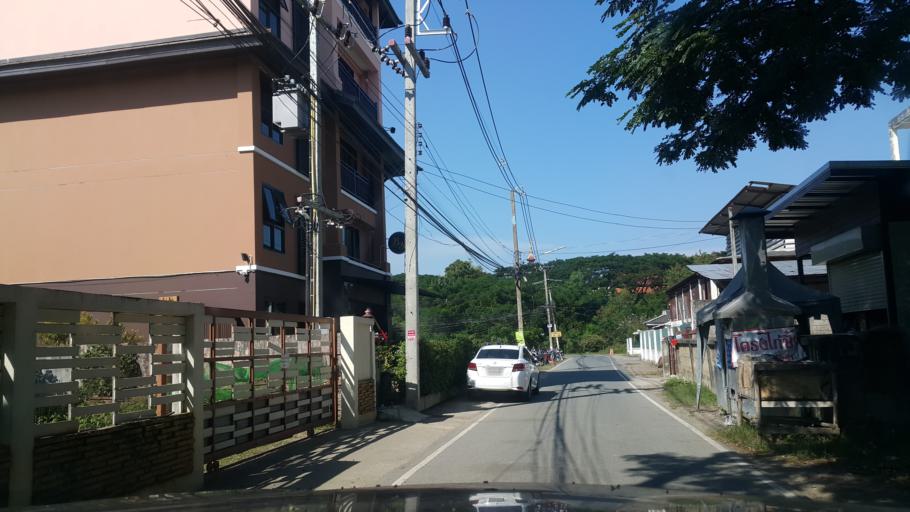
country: TH
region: Chiang Mai
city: Chiang Mai
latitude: 18.7760
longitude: 99.0354
